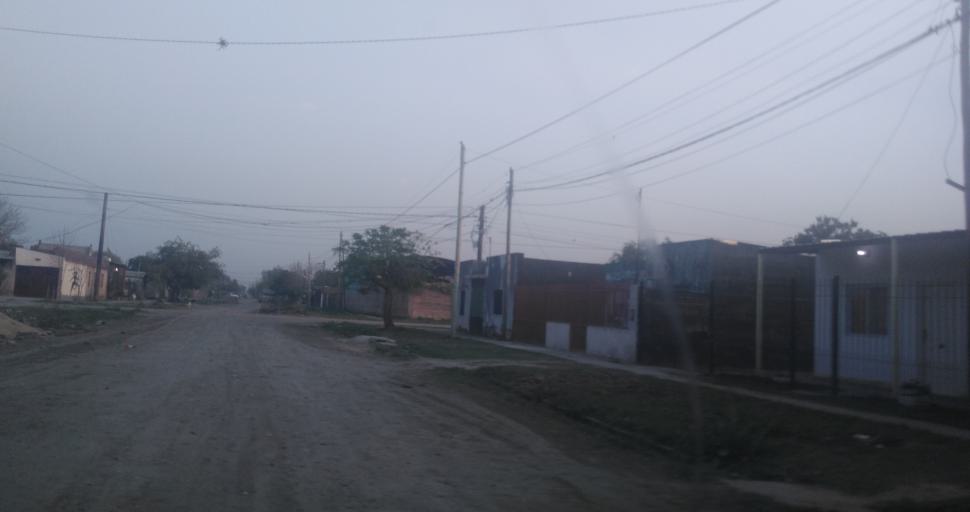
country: AR
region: Chaco
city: Resistencia
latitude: -27.4738
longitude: -59.0075
